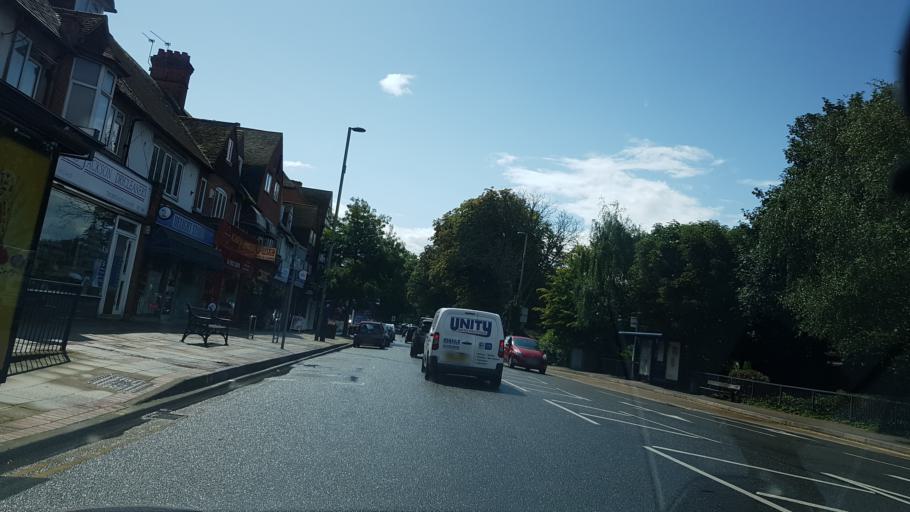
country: GB
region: England
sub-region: Surrey
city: West Byfleet
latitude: 51.3370
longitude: -0.5049
